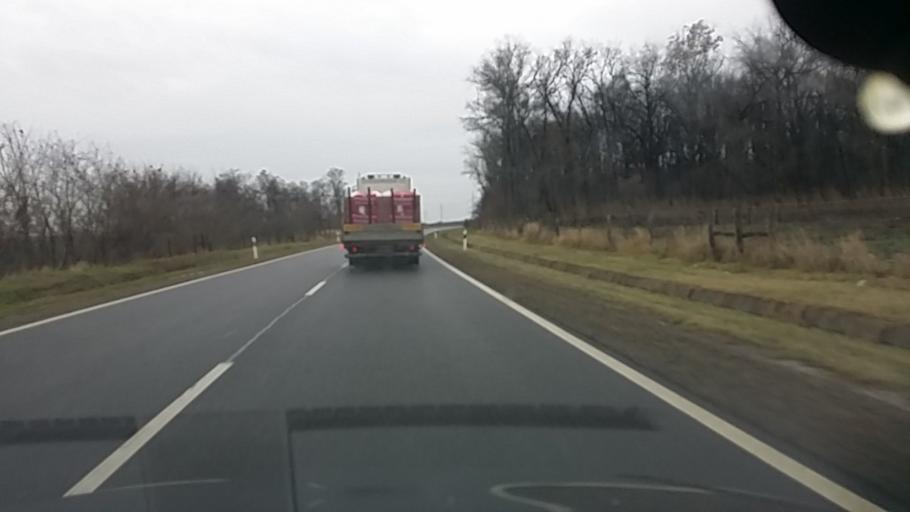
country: HU
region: Hajdu-Bihar
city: Hajduhadhaz
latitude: 47.6354
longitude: 21.6474
